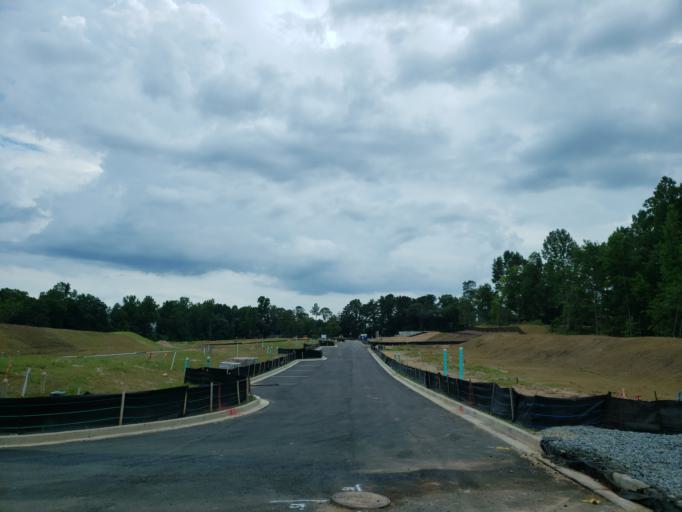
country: US
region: Georgia
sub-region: Cherokee County
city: Woodstock
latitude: 34.1154
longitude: -84.5267
